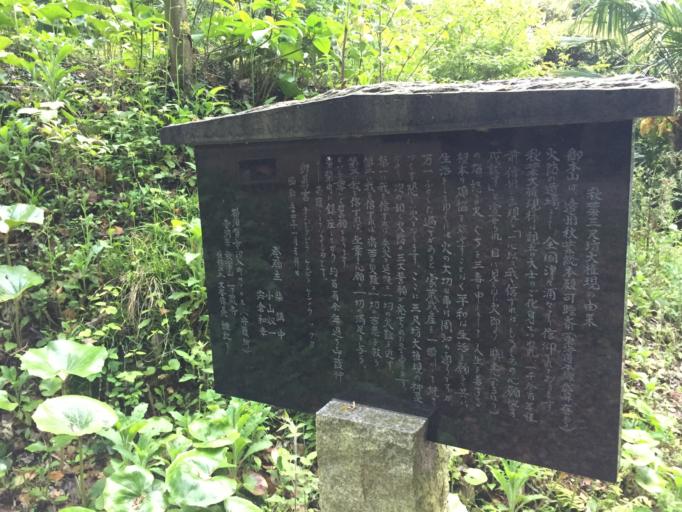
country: JP
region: Kanagawa
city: Yokosuka
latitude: 35.3449
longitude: 139.6363
